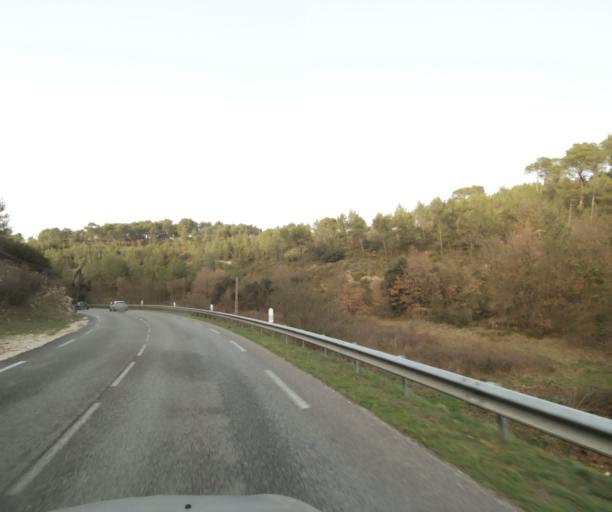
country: FR
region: Provence-Alpes-Cote d'Azur
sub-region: Departement des Bouches-du-Rhone
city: Rognes
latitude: 43.6708
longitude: 5.3530
